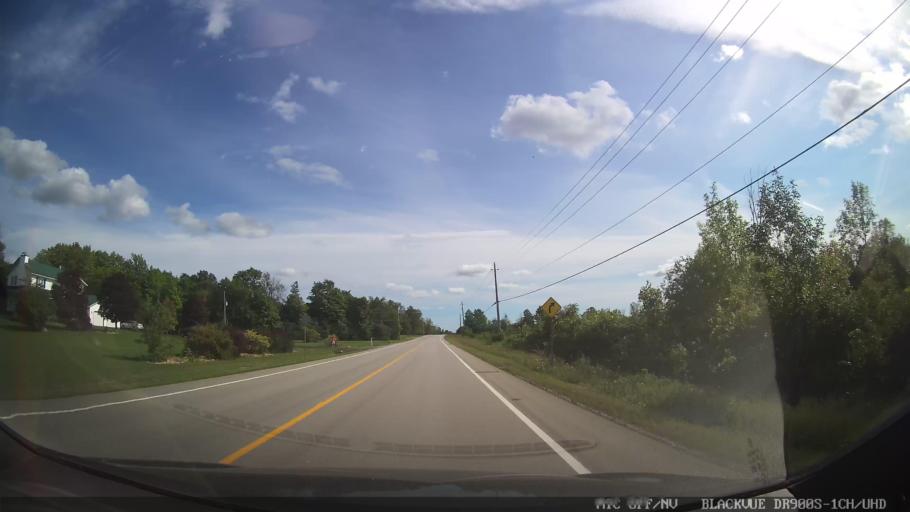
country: CA
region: Ontario
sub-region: Lanark County
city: Smiths Falls
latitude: 44.9363
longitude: -75.9629
